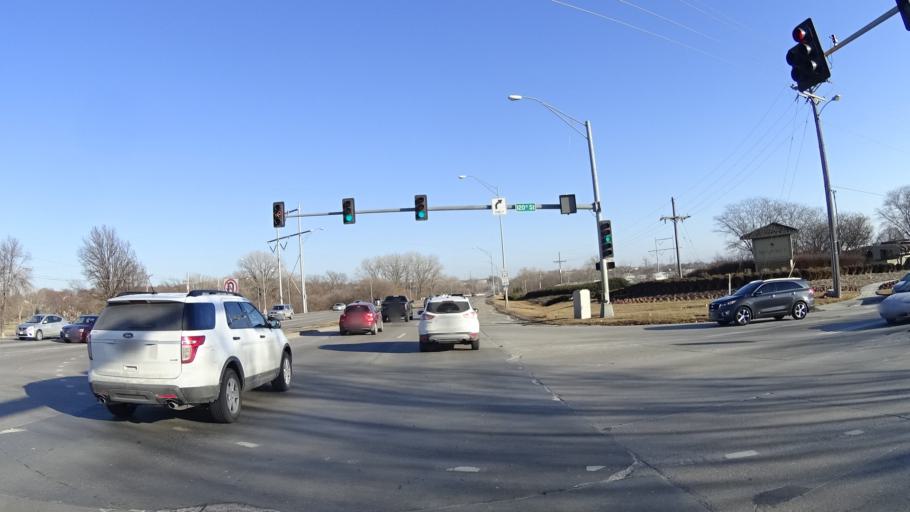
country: US
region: Nebraska
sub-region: Douglas County
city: Bennington
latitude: 41.2920
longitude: -96.1009
